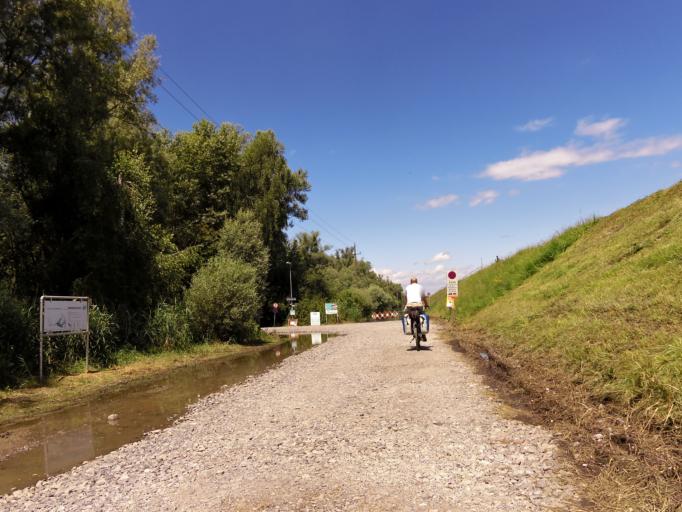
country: AT
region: Vorarlberg
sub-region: Politischer Bezirk Bregenz
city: Fussach
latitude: 47.4893
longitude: 9.6681
